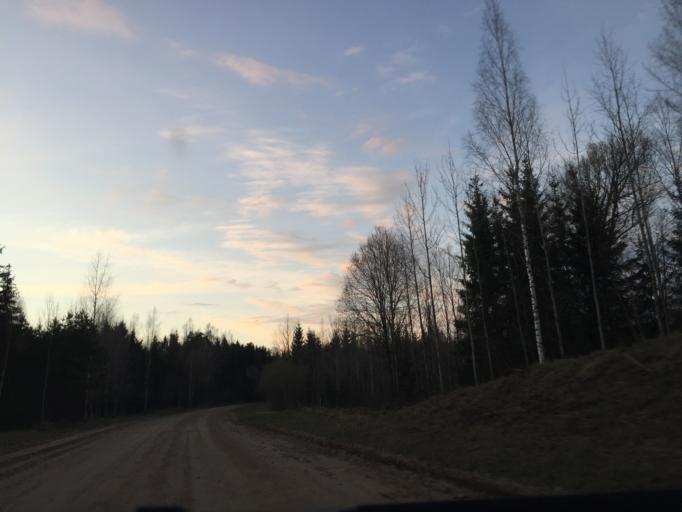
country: LV
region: Aluksnes Rajons
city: Aluksne
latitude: 57.3026
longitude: 26.9135
